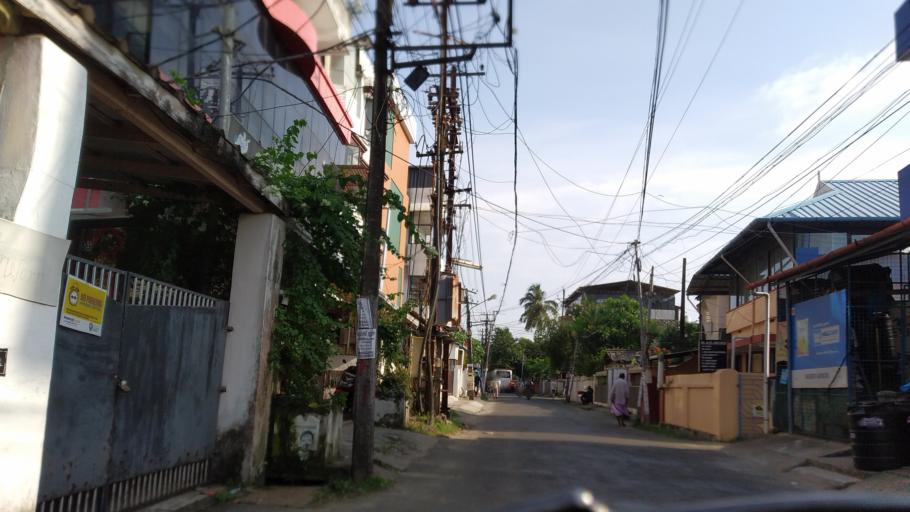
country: IN
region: Kerala
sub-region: Ernakulam
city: Cochin
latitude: 10.0004
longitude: 76.2841
